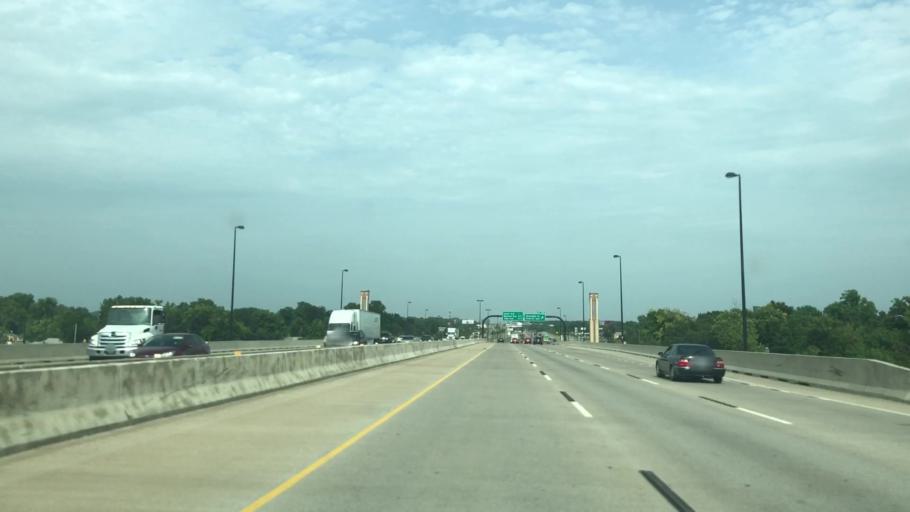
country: US
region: Oklahoma
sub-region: Tulsa County
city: Tulsa
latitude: 36.0898
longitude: -95.9868
